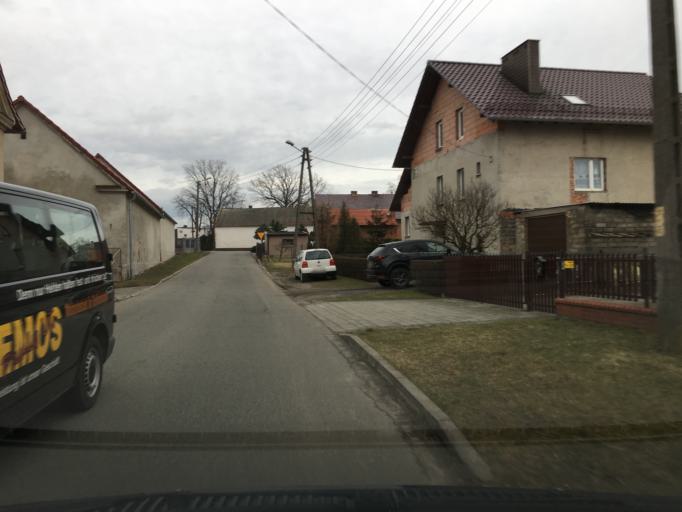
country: PL
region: Opole Voivodeship
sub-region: Powiat kedzierzynsko-kozielski
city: Wiekszyce
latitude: 50.3529
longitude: 18.1208
